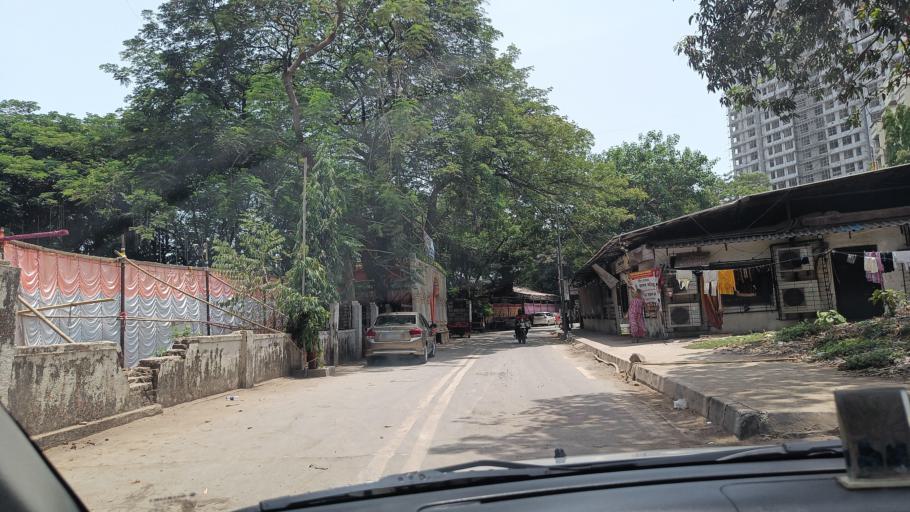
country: IN
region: Maharashtra
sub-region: Mumbai Suburban
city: Mumbai
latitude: 19.0522
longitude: 72.8769
